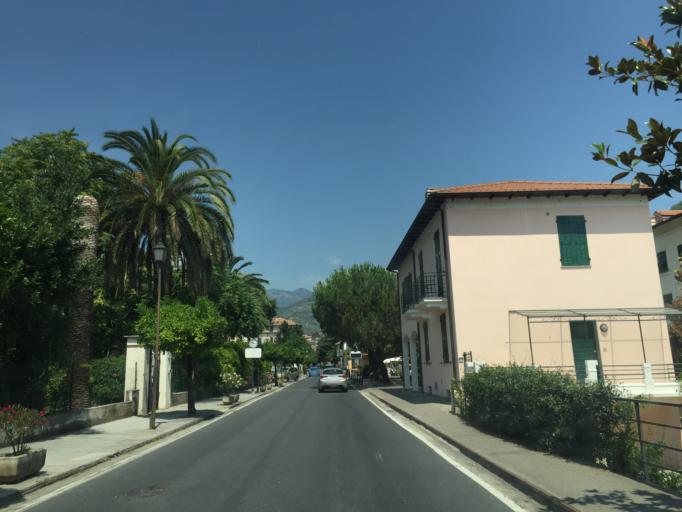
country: IT
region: Liguria
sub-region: Provincia di Imperia
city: Dolceacqua
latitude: 43.8472
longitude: 7.6239
